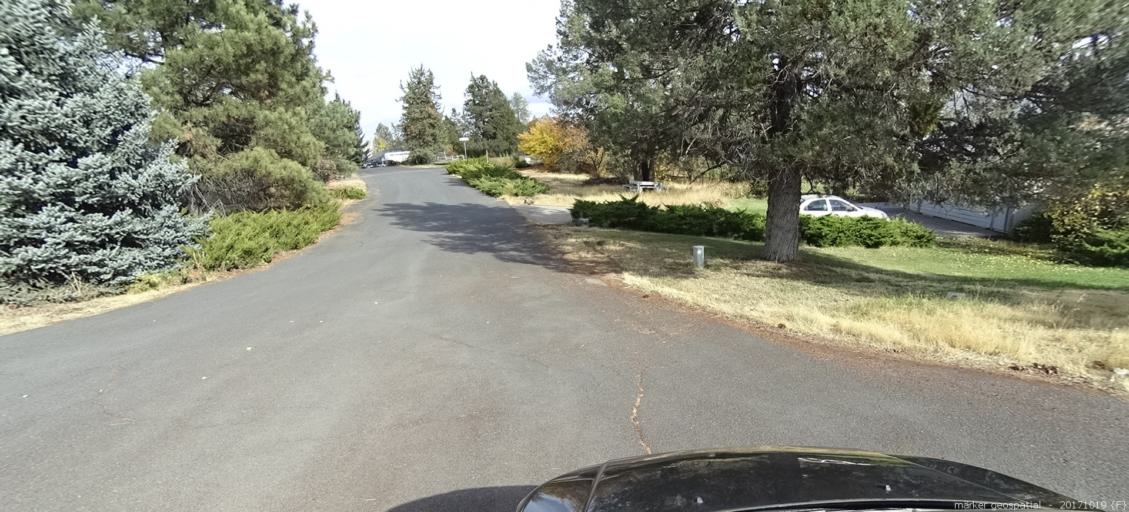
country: US
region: California
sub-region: Shasta County
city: Burney
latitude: 40.9984
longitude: -121.4501
